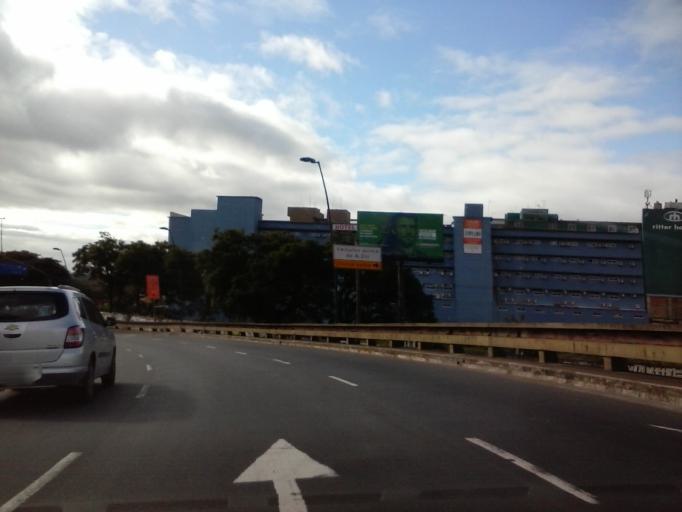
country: BR
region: Rio Grande do Sul
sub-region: Porto Alegre
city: Porto Alegre
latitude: -30.0257
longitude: -51.2189
